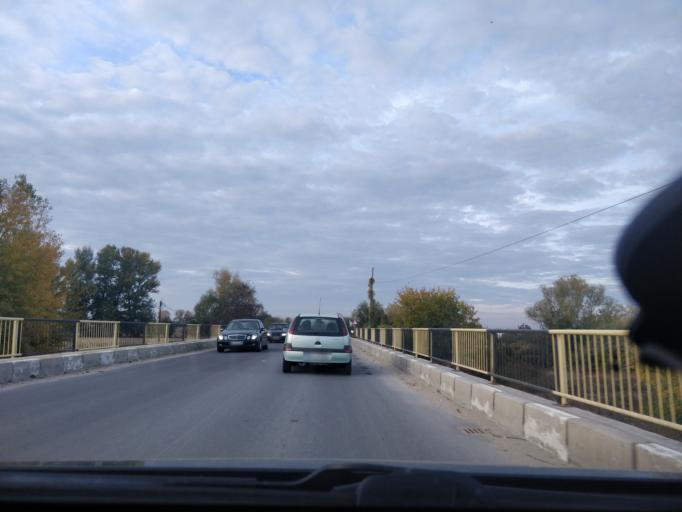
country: RO
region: Giurgiu
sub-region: Comuna Bolintin Vale
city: Malu Spart
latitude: 44.4378
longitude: 25.7318
